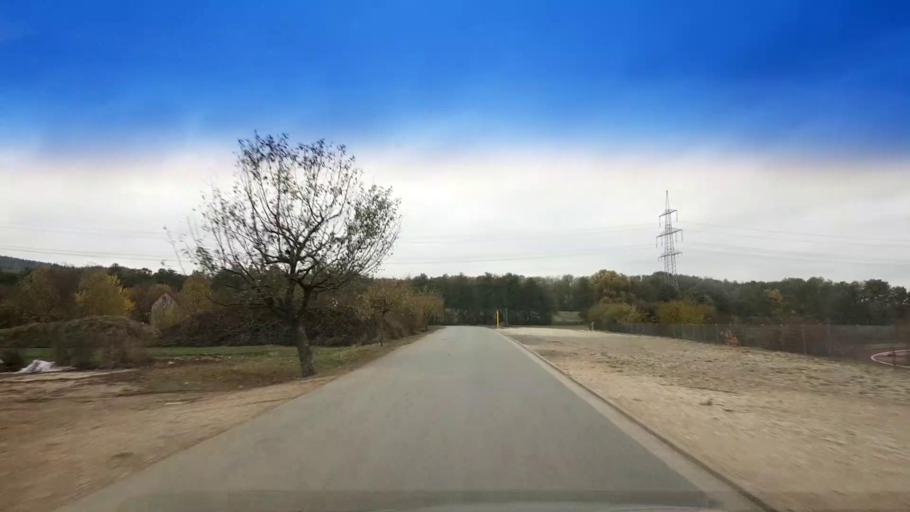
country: DE
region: Bavaria
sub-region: Upper Franconia
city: Schesslitz
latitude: 49.9698
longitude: 11.0313
